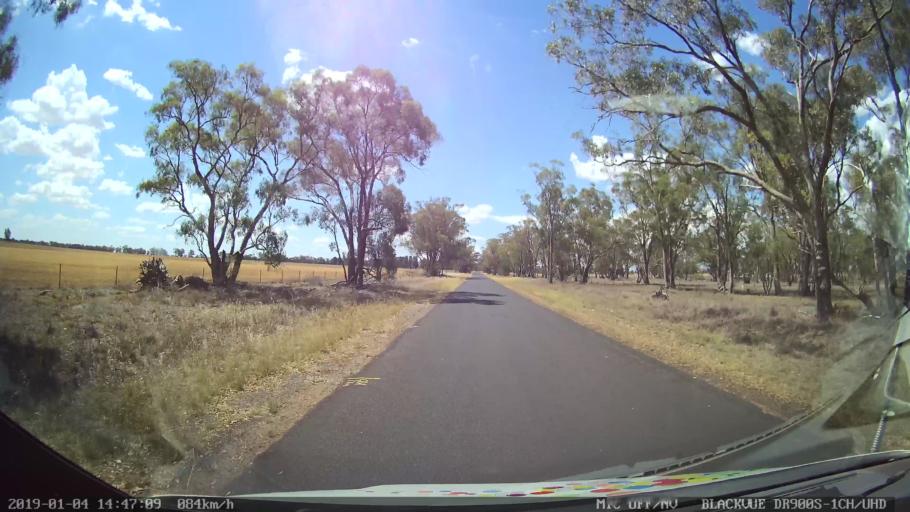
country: AU
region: New South Wales
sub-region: Dubbo Municipality
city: Dubbo
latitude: -32.0725
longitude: 148.6596
